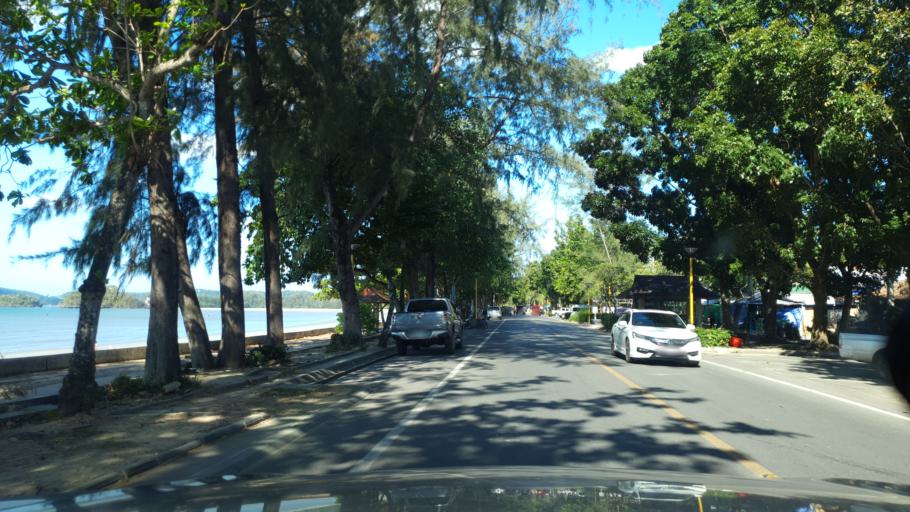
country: TH
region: Phangnga
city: Ban Ao Nang
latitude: 8.0433
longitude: 98.8092
